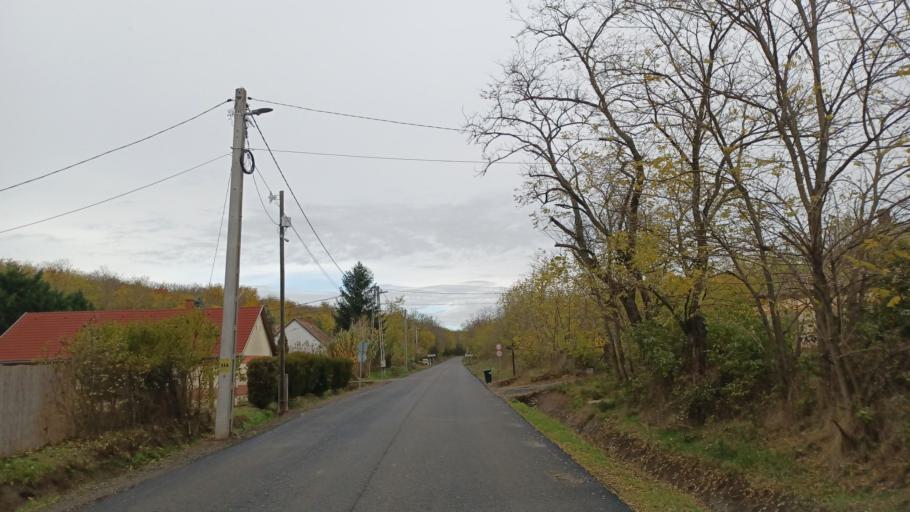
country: HU
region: Tolna
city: Dunaszentgyorgy
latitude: 46.5300
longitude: 18.7657
